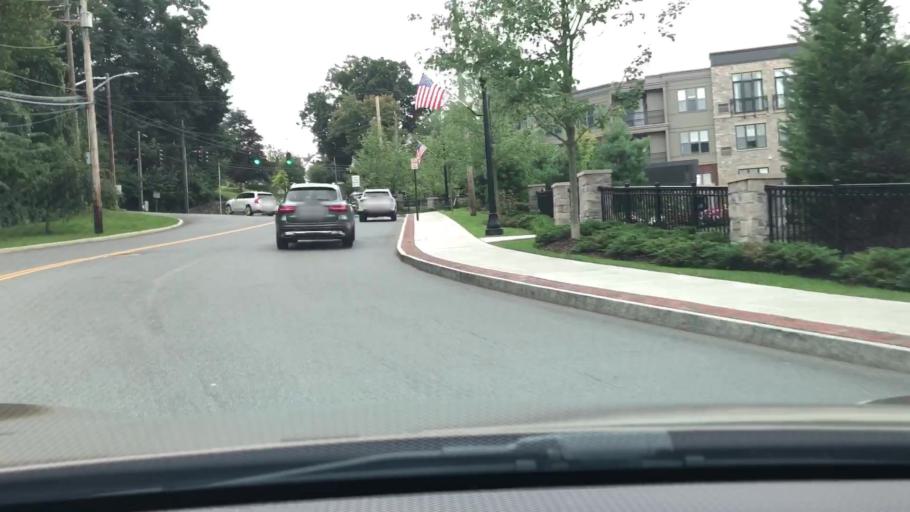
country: US
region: New York
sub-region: Westchester County
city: Tuckahoe
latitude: 40.9489
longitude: -73.8223
